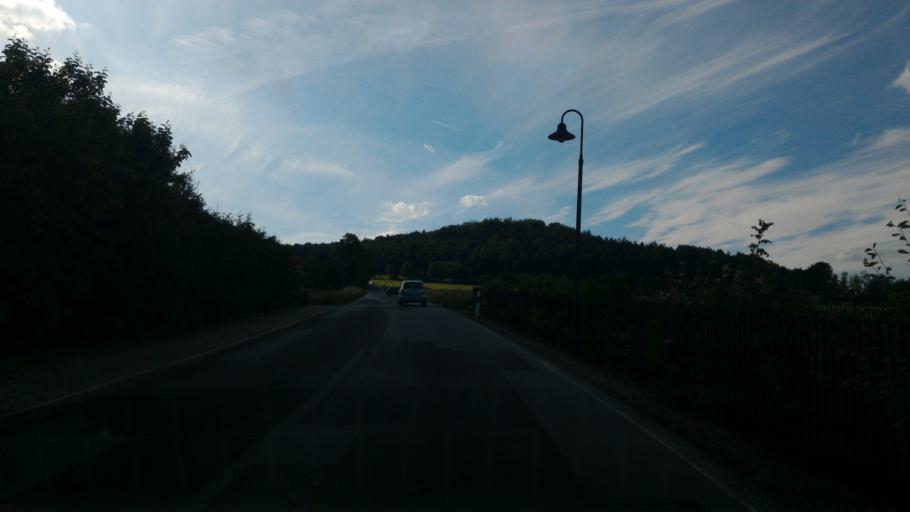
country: DE
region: Saxony
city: Bertsdorf-Hoernitz
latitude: 50.8808
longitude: 14.7216
